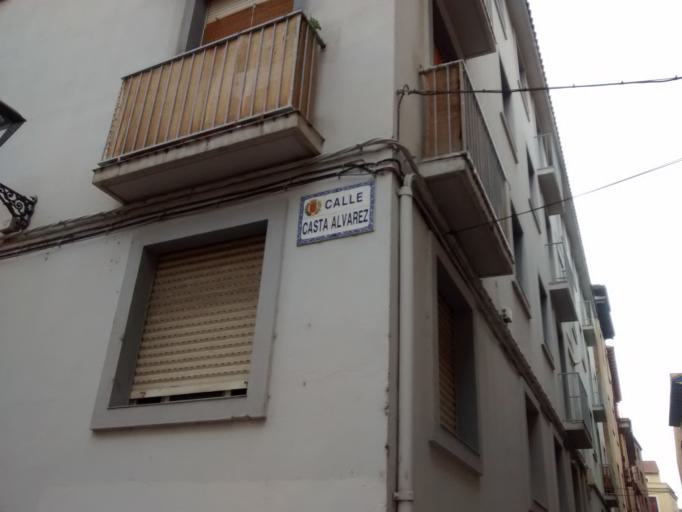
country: ES
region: Aragon
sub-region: Provincia de Zaragoza
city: Zaragoza
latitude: 41.6574
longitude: -0.8867
